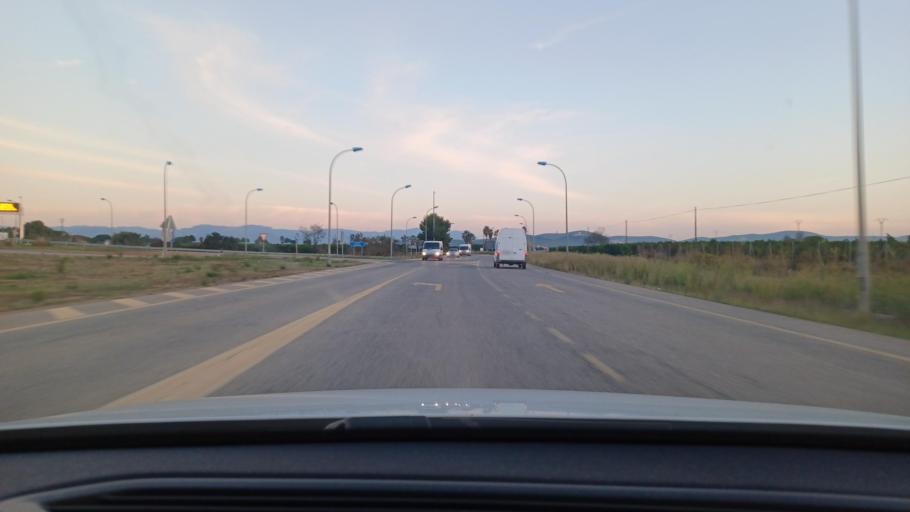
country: ES
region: Catalonia
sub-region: Provincia de Tarragona
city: Ulldecona
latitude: 40.5532
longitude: 0.4321
